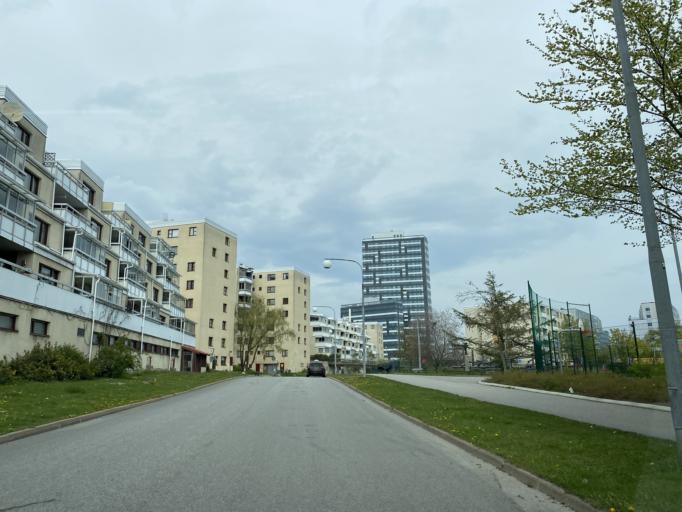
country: SE
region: Stockholm
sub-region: Stockholms Kommun
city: Kista
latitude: 59.4018
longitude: 17.9389
